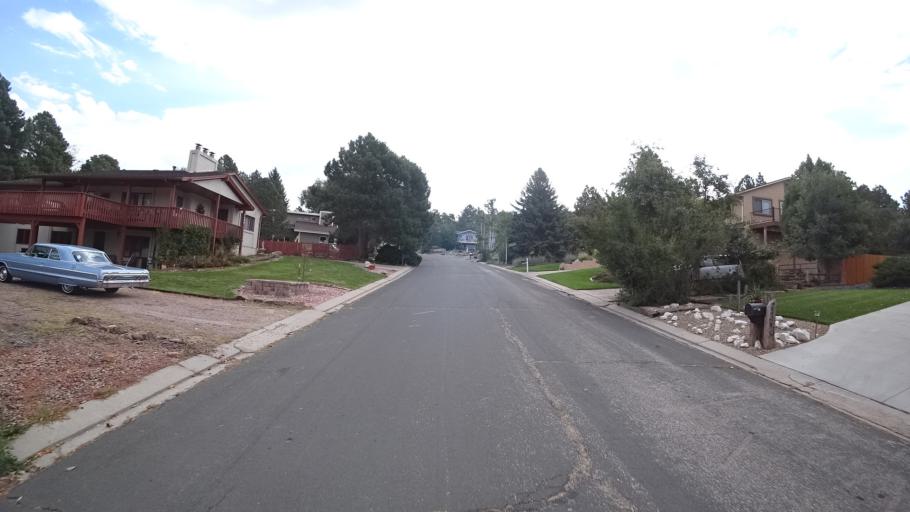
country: US
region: Colorado
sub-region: El Paso County
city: Cimarron Hills
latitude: 38.8689
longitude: -104.7518
